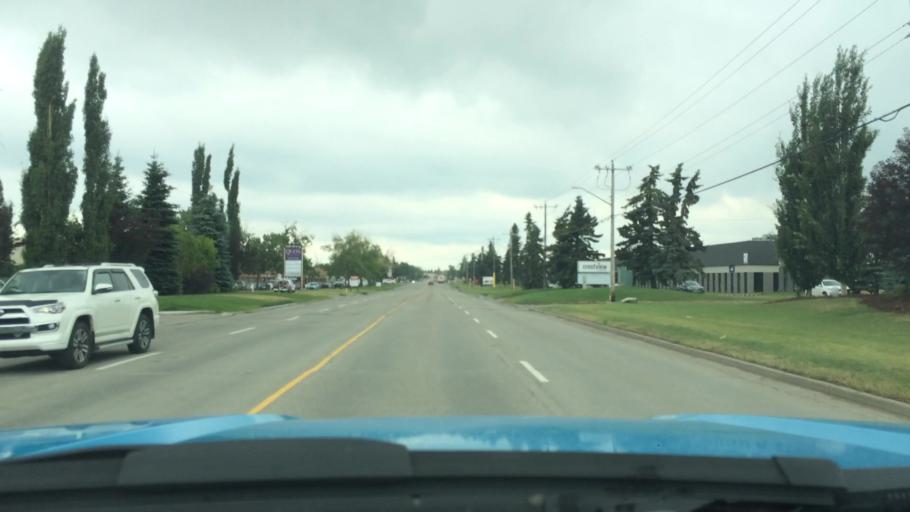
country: CA
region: Alberta
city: Calgary
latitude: 51.0867
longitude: -114.0116
